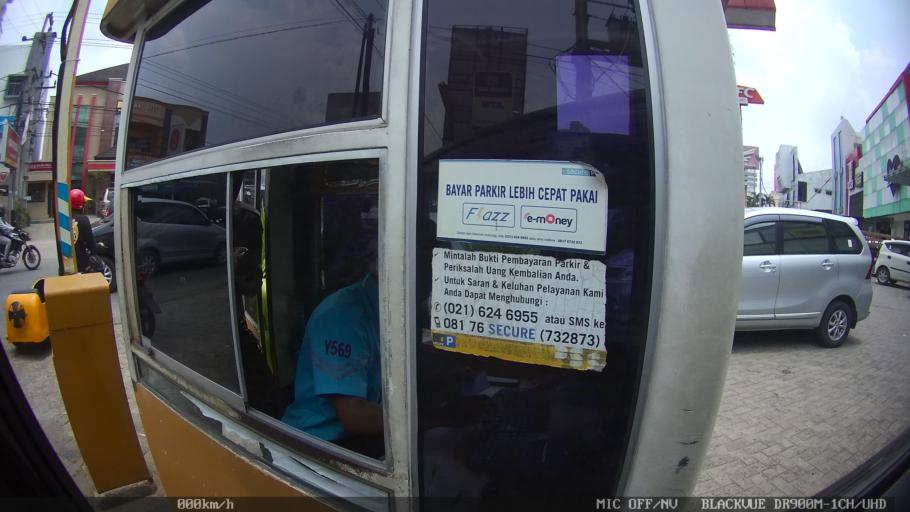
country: ID
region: Lampung
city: Pringsewu
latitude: -5.3572
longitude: 104.9856
